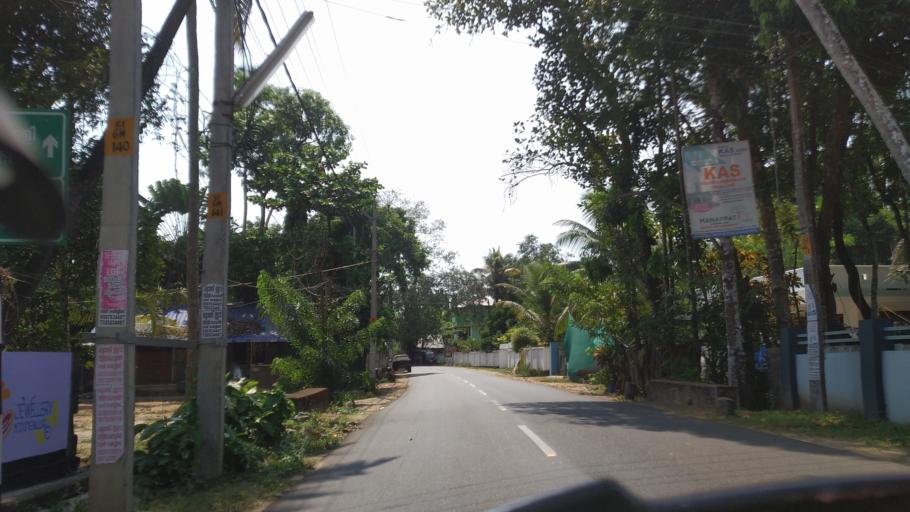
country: IN
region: Kerala
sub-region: Thrissur District
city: Kodungallur
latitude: 10.2067
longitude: 76.1834
